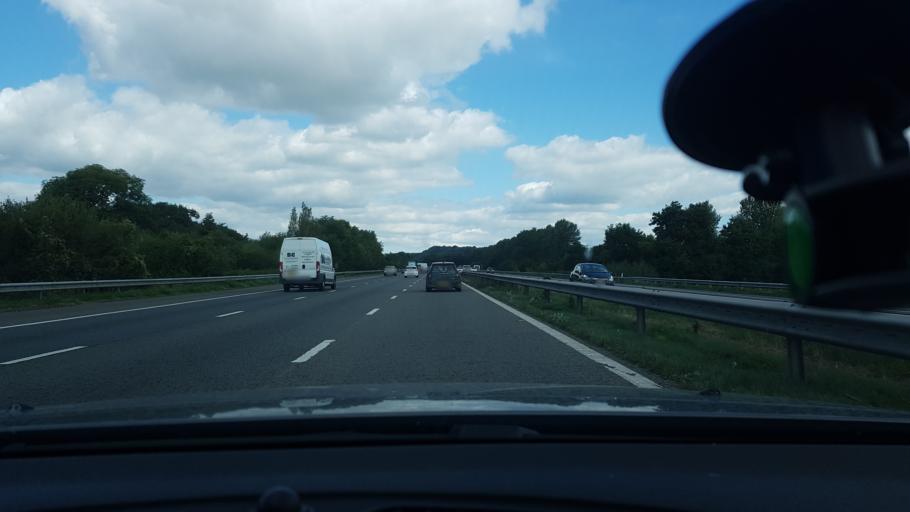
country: GB
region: England
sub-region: Devon
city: Bradninch
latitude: 50.8220
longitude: -3.4070
